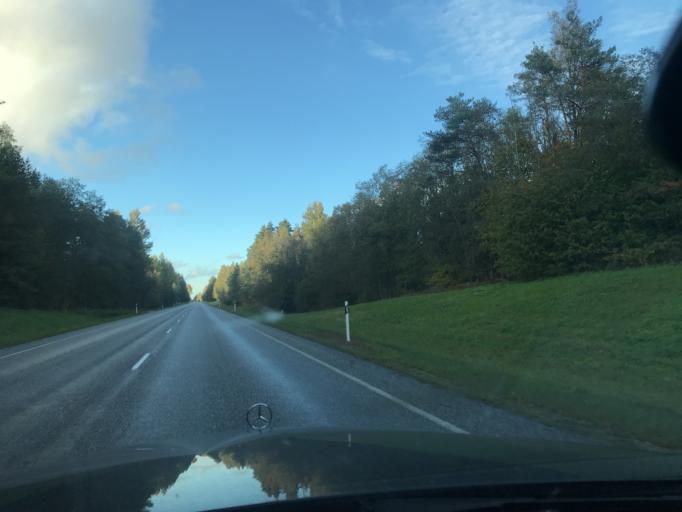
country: RU
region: Pskov
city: Pechory
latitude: 57.6615
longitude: 27.3310
